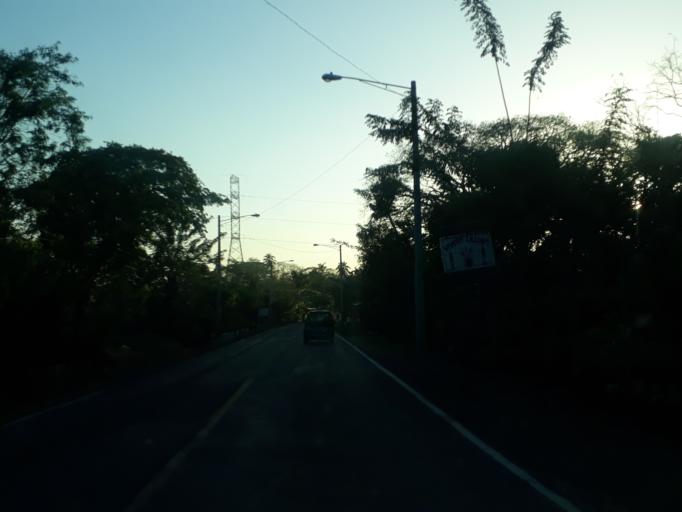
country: NI
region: Masaya
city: San Juan de Oriente
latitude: 11.9084
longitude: -86.0827
